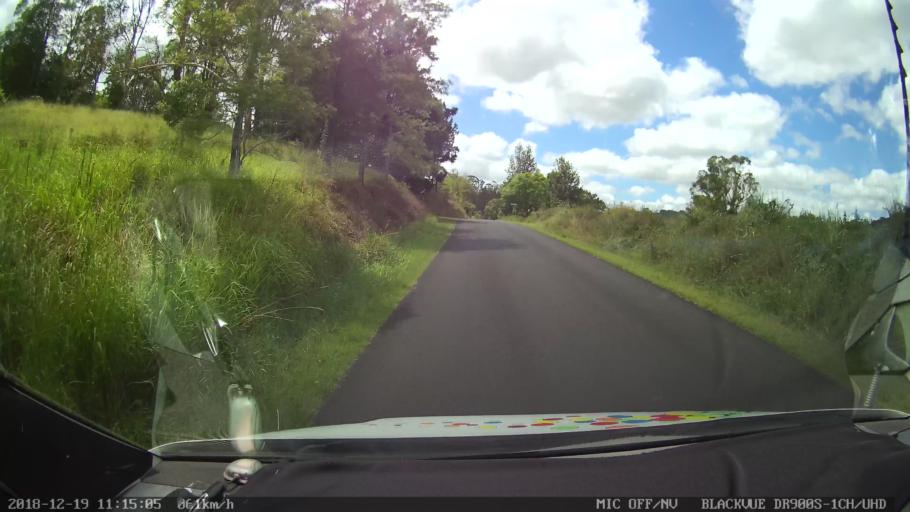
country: AU
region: New South Wales
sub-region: Lismore Municipality
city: Nimbin
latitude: -28.6652
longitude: 153.2761
